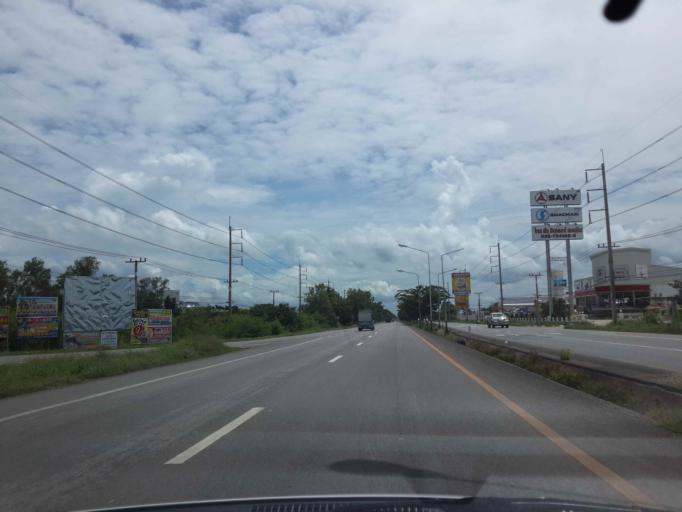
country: TH
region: Ratchaburi
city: Pak Tho
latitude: 13.3918
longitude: 99.8168
